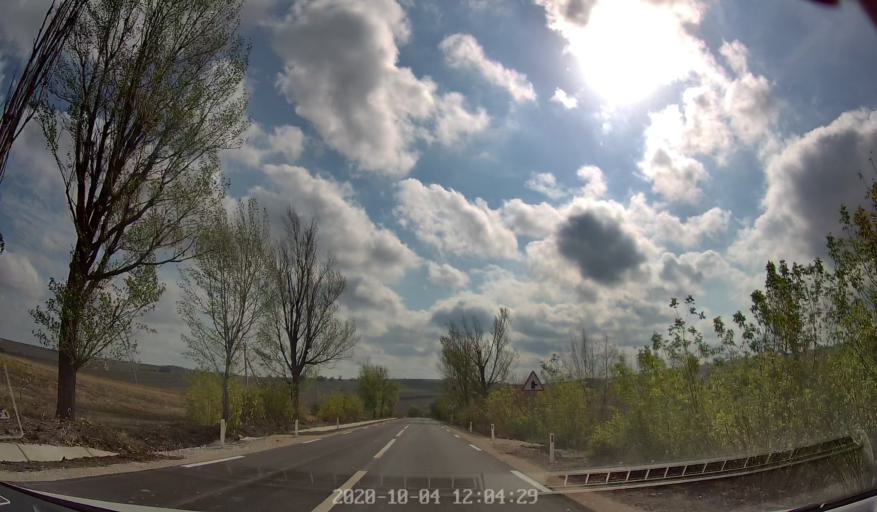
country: MD
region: Rezina
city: Saharna
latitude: 47.6034
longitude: 28.9434
